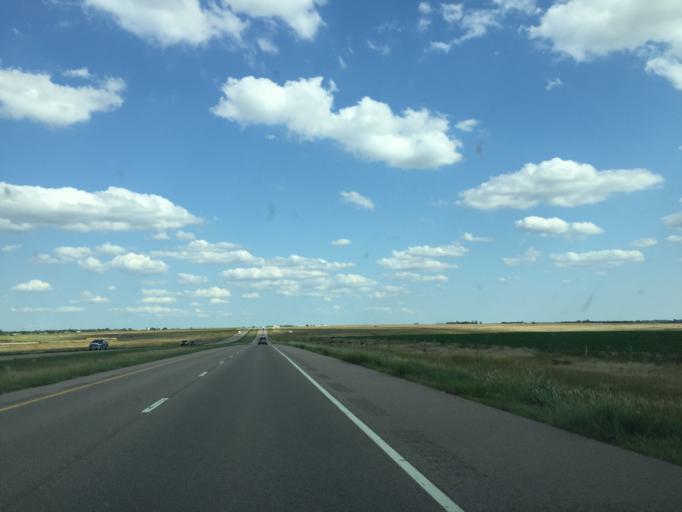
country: US
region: Kansas
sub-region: Gove County
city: Gove
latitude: 39.0738
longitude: -100.2759
